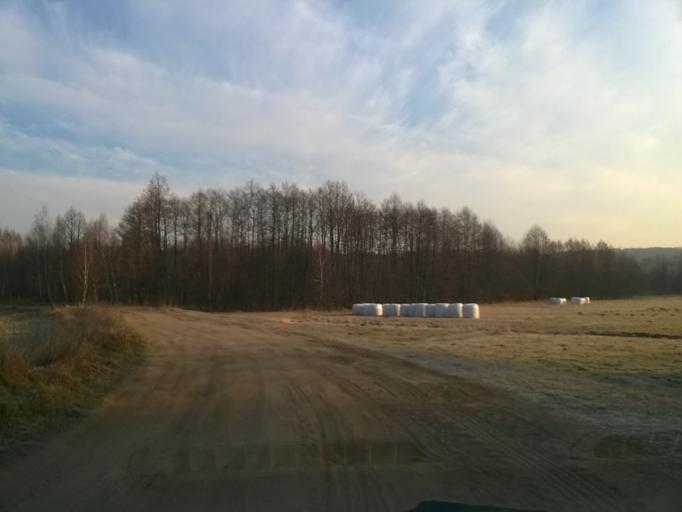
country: PL
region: Kujawsko-Pomorskie
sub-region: Powiat tucholski
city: Kesowo
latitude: 53.5062
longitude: 17.7055
